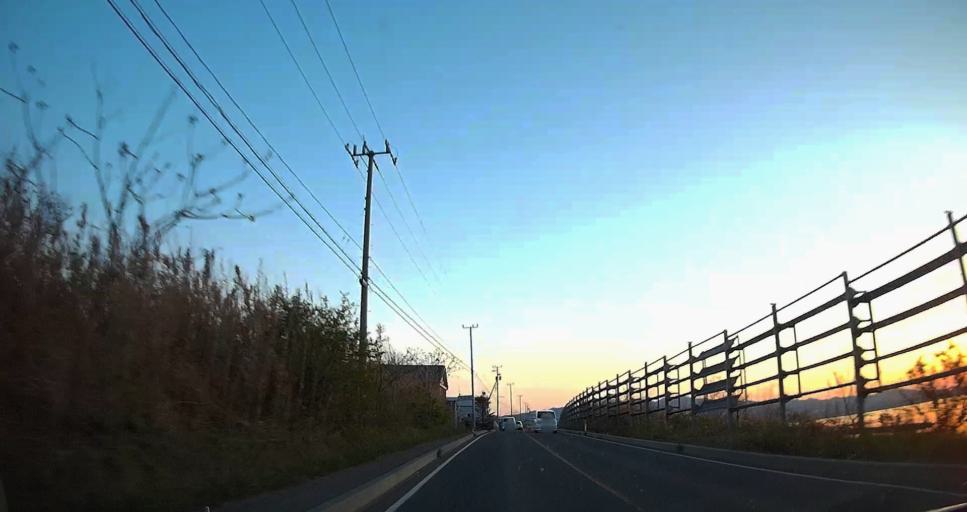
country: JP
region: Aomori
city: Misawa
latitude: 40.8792
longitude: 141.1492
